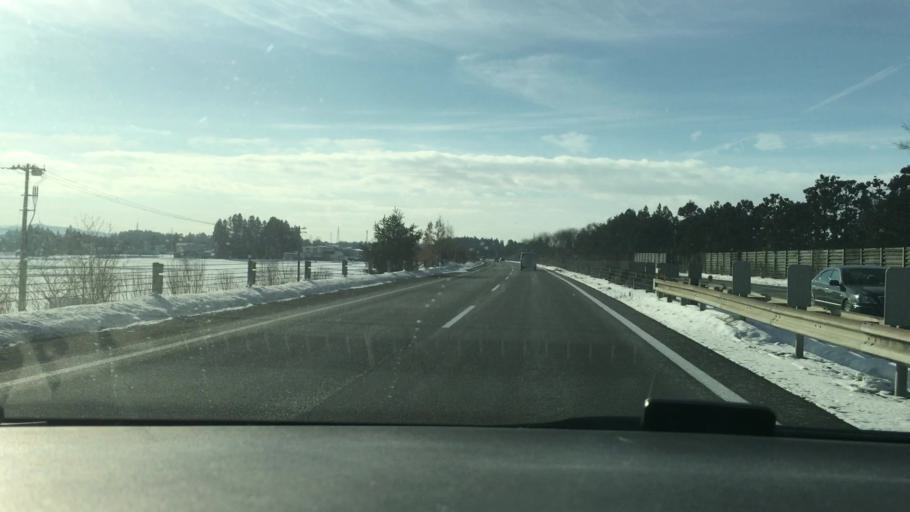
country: JP
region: Iwate
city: Hanamaki
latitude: 39.3575
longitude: 141.0895
